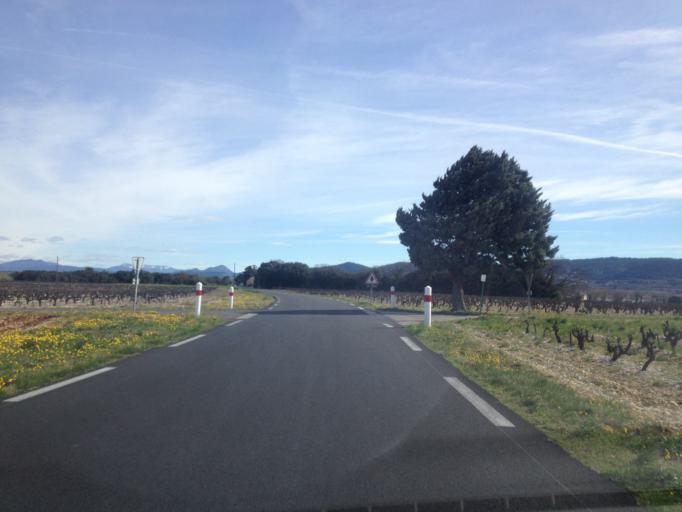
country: FR
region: Provence-Alpes-Cote d'Azur
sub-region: Departement du Vaucluse
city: Violes
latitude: 44.1925
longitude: 4.9698
